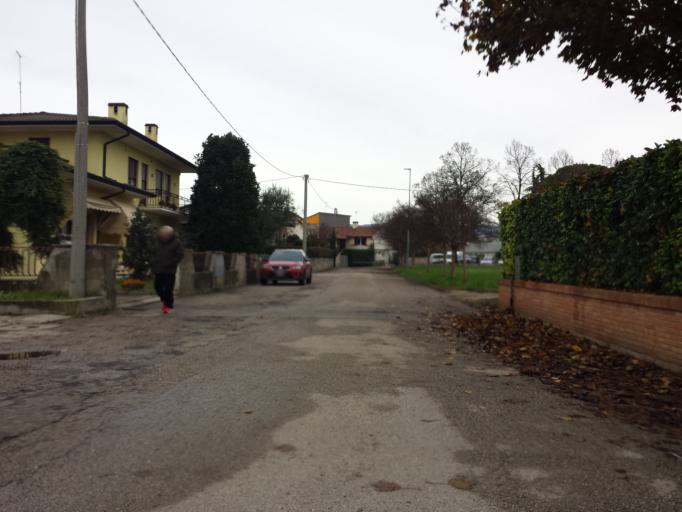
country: IT
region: Veneto
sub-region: Provincia di Vicenza
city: Sandrigo
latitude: 45.6633
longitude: 11.6034
